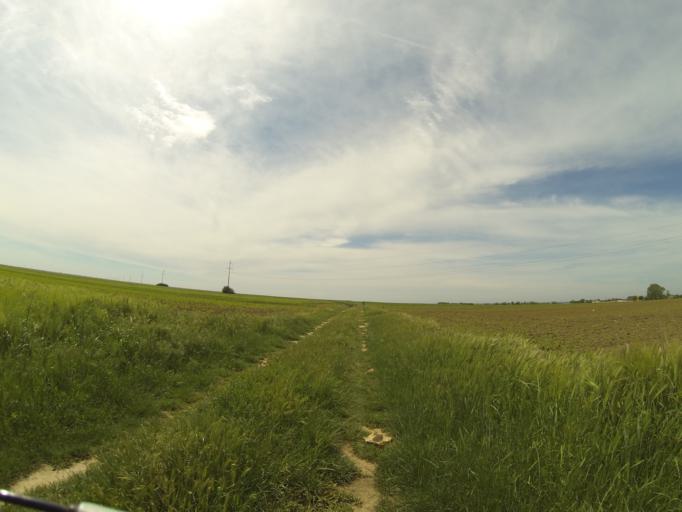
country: RO
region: Dolj
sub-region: Comuna Ghindeni
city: Ghindeni
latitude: 44.2150
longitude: 23.9390
